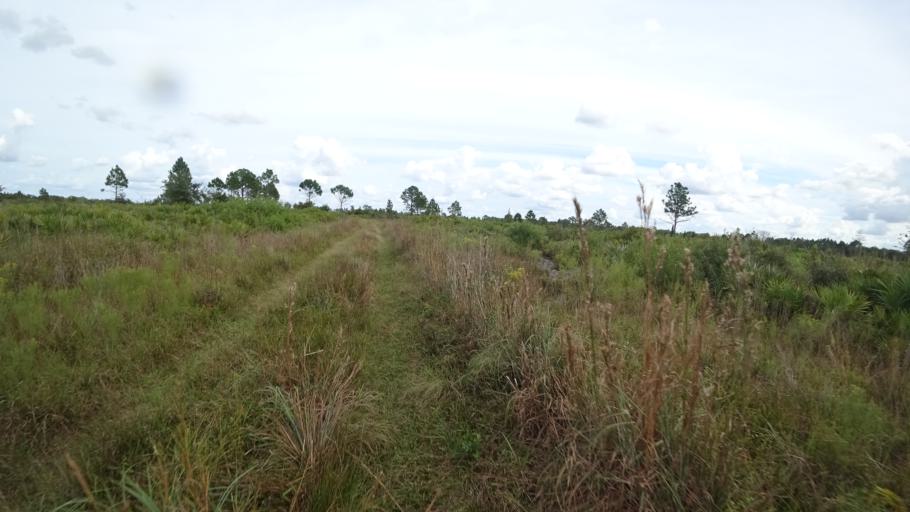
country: US
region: Florida
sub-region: Hillsborough County
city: Wimauma
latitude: 27.5588
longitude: -82.1275
